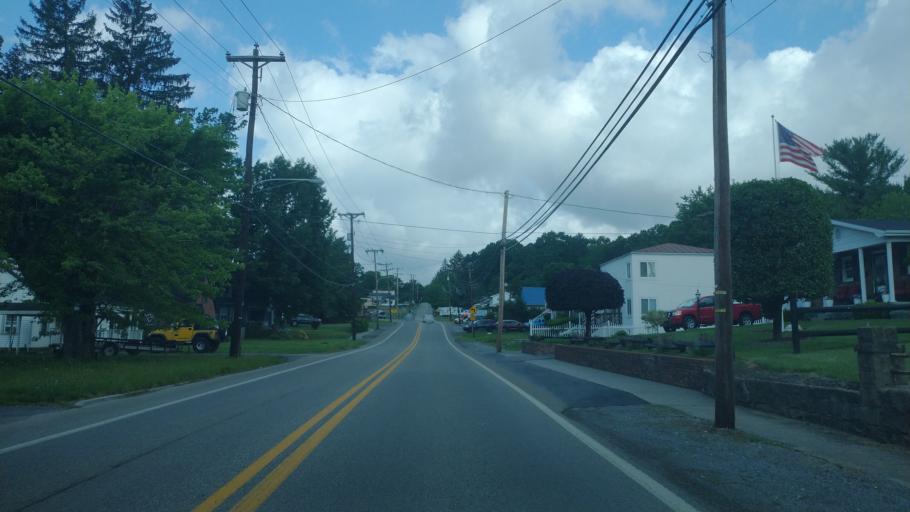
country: US
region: West Virginia
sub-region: Mercer County
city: Princeton
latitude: 37.3673
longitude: -81.1076
